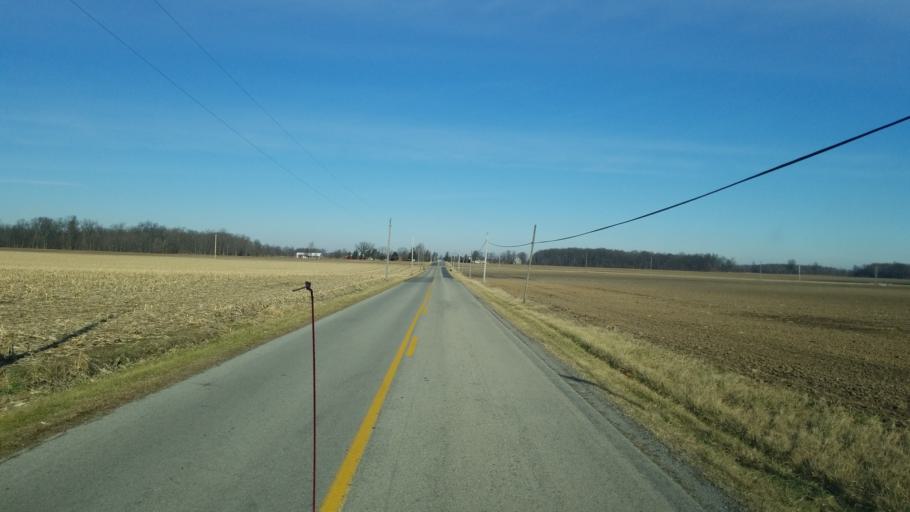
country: US
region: Ohio
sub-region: Allen County
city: Bluffton
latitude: 40.8601
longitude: -83.8991
